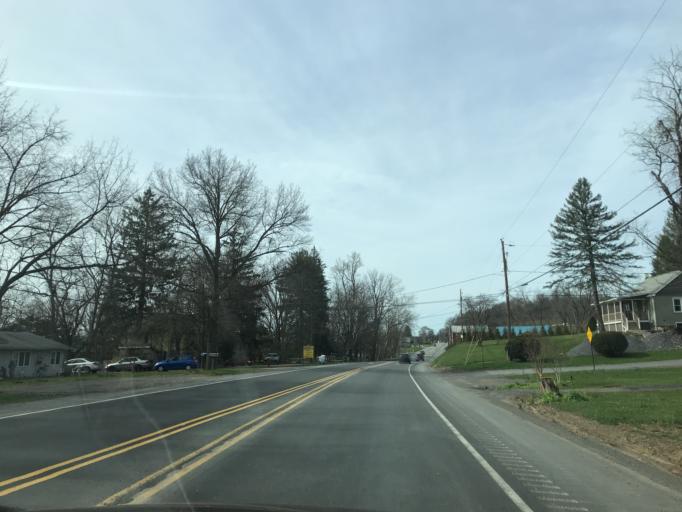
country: US
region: Pennsylvania
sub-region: Northumberland County
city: Northumberland
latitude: 40.9197
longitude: -76.8441
